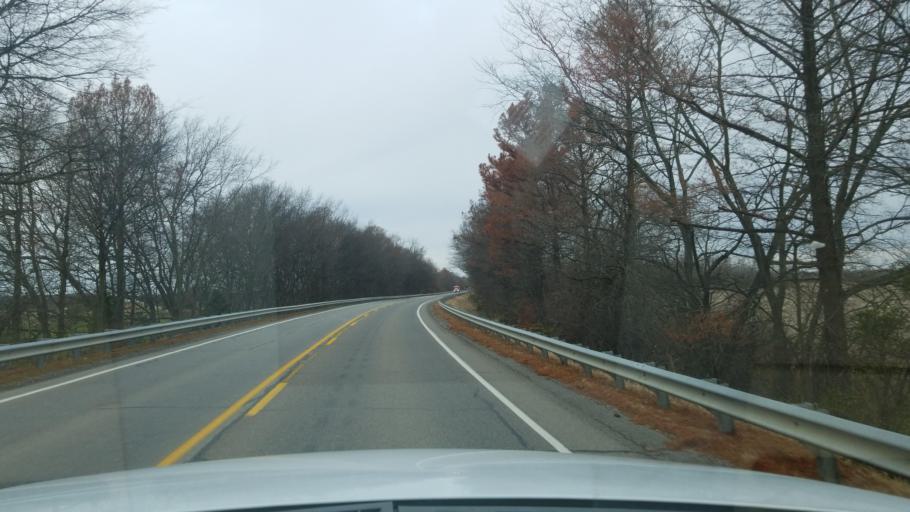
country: US
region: Indiana
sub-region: Posey County
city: Mount Vernon
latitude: 37.9305
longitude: -88.0016
